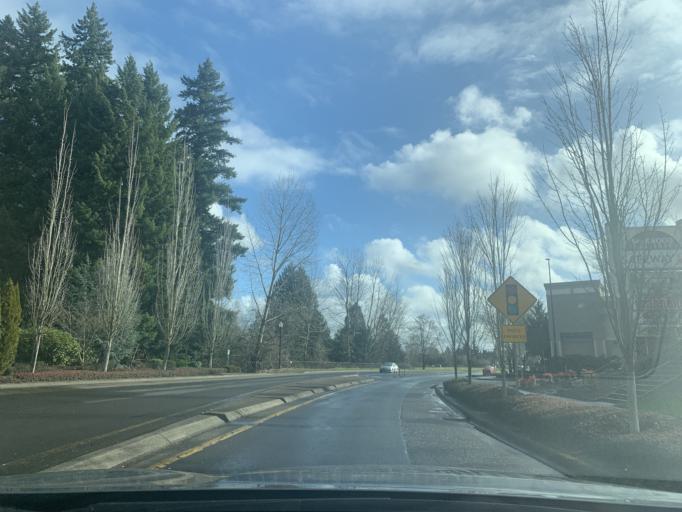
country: US
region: Oregon
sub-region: Washington County
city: Sherwood
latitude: 45.3713
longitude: -122.8456
